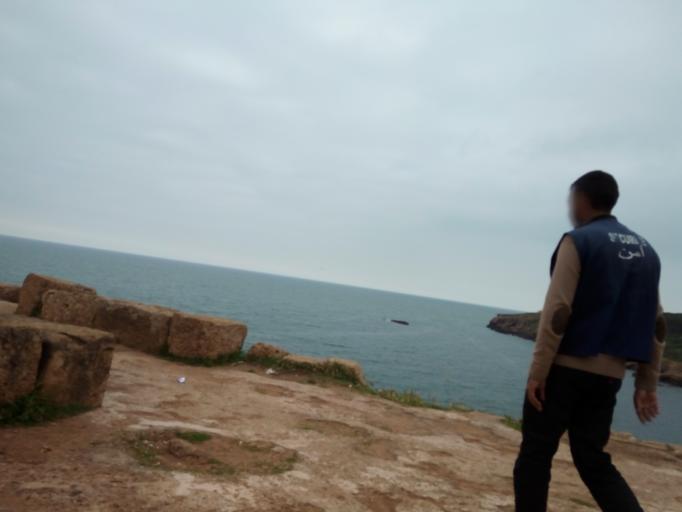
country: DZ
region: Tipaza
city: Tipasa
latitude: 36.5950
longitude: 2.4410
